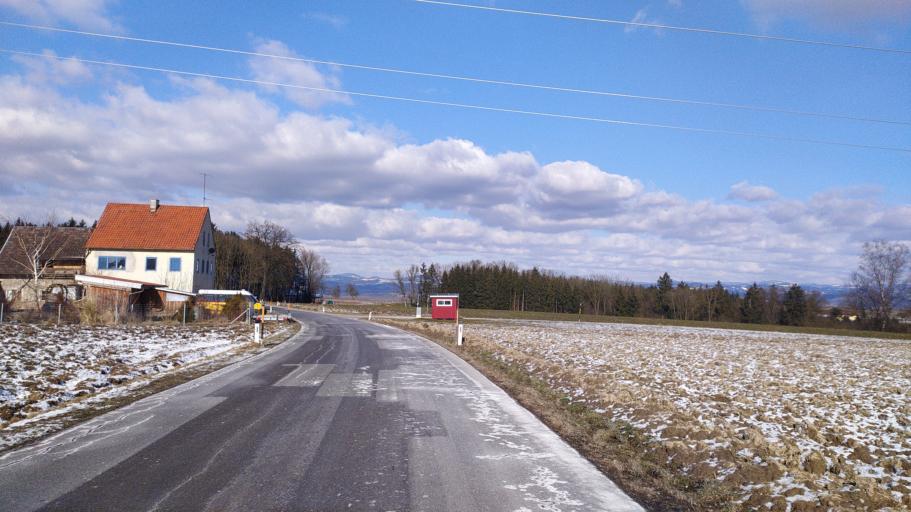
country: AT
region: Lower Austria
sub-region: Politischer Bezirk Amstetten
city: Zeillern
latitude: 48.1401
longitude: 14.7393
